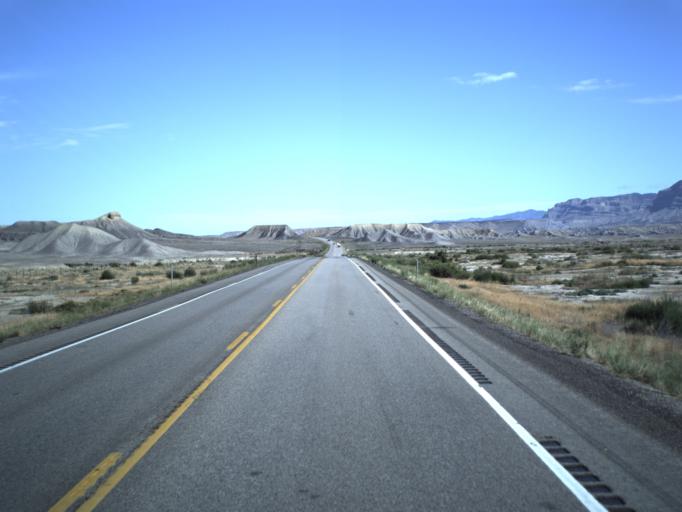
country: US
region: Utah
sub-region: Carbon County
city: East Carbon City
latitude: 39.3272
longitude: -110.3673
